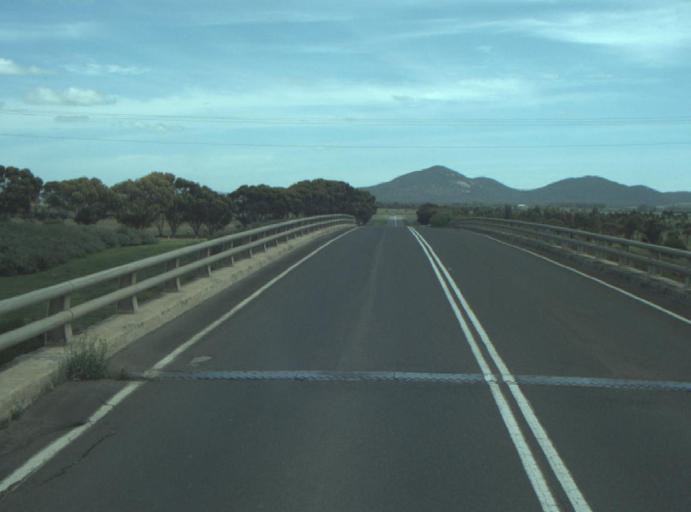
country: AU
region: Victoria
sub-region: Wyndham
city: Little River
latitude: -38.0142
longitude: 144.4670
